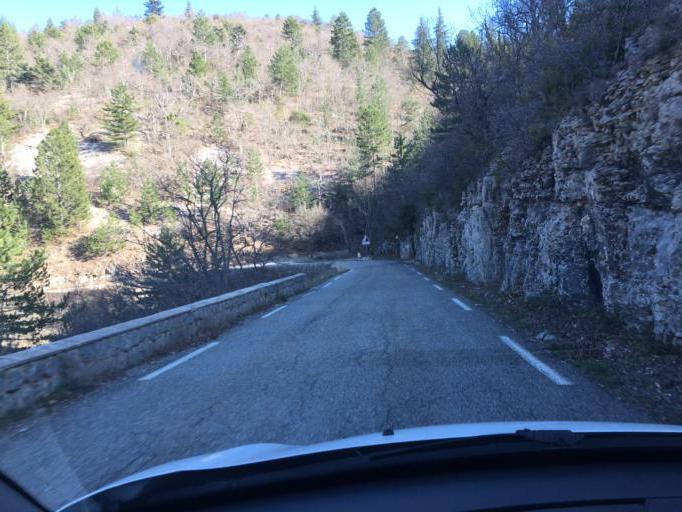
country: FR
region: Provence-Alpes-Cote d'Azur
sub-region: Departement du Vaucluse
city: Villes-sur-Auzon
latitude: 44.0640
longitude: 5.3213
